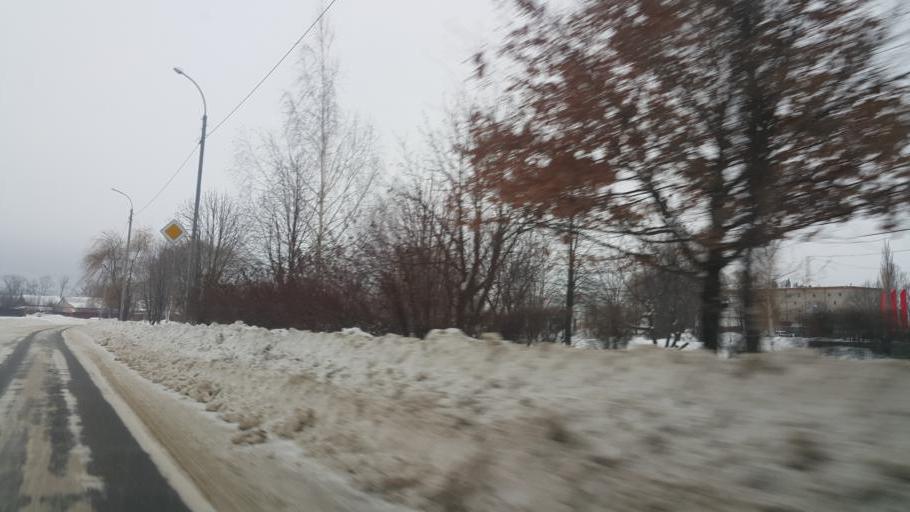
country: RU
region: Tambov
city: Bokino
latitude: 52.6498
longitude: 41.4532
